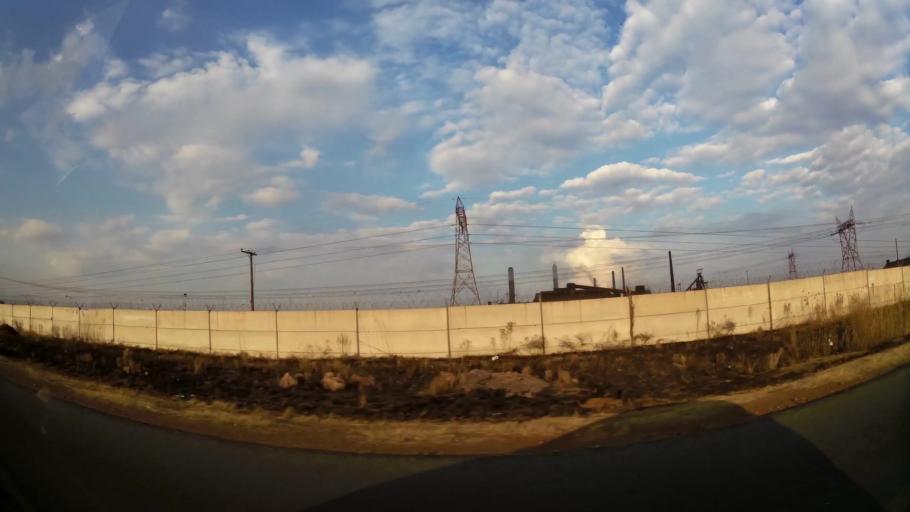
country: ZA
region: Gauteng
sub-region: Sedibeng District Municipality
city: Vanderbijlpark
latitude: -26.6543
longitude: 27.8026
